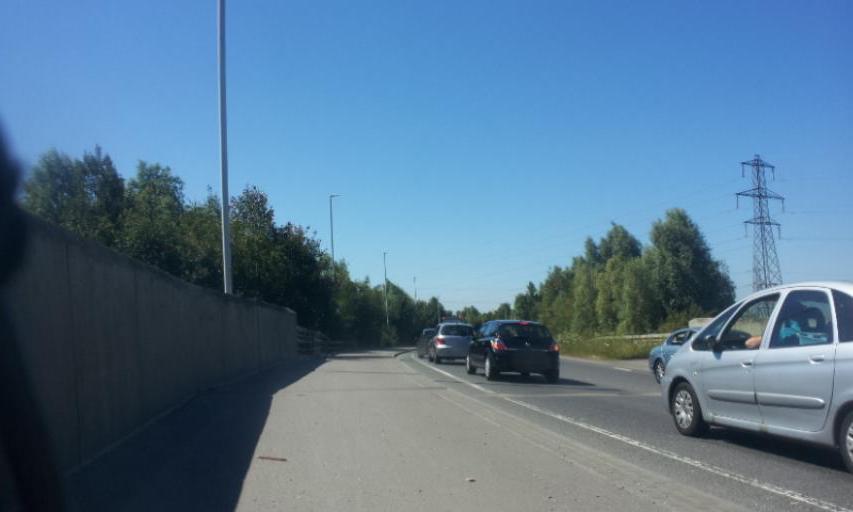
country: GB
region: England
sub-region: Kent
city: Sittingbourne
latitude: 51.3666
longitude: 0.7380
